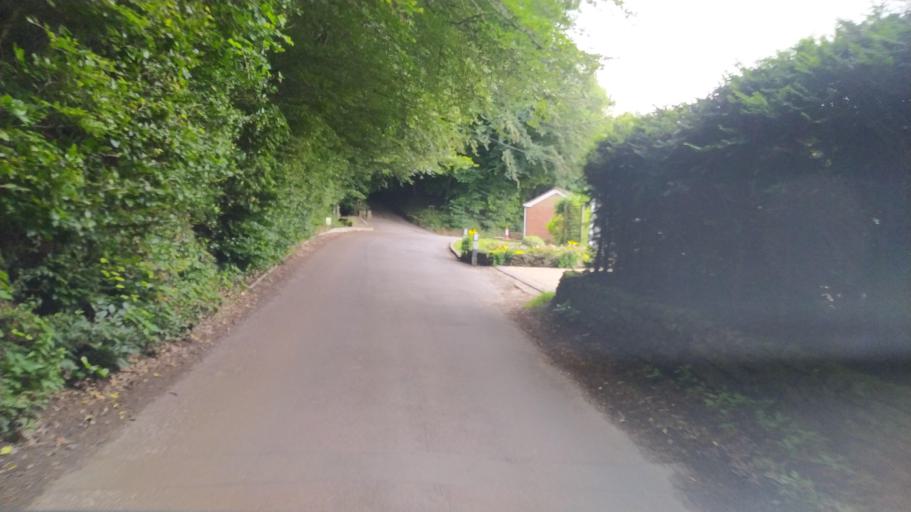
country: GB
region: England
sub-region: Hampshire
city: Liphook
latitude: 51.0909
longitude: -0.8032
